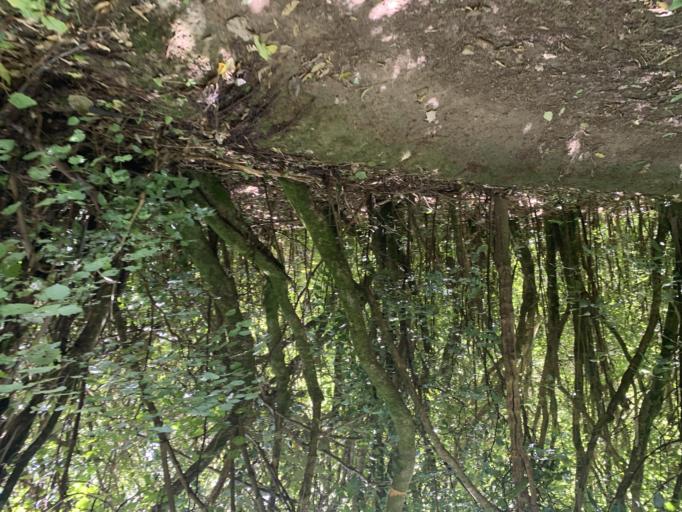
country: NZ
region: Wellington
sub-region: Wellington City
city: Brooklyn
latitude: -41.2985
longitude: 174.7540
